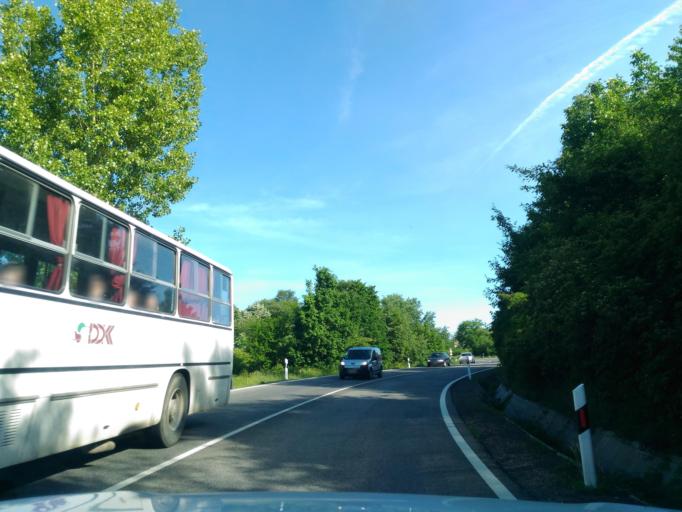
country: HU
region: Baranya
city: Komlo
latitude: 46.1748
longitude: 18.2600
